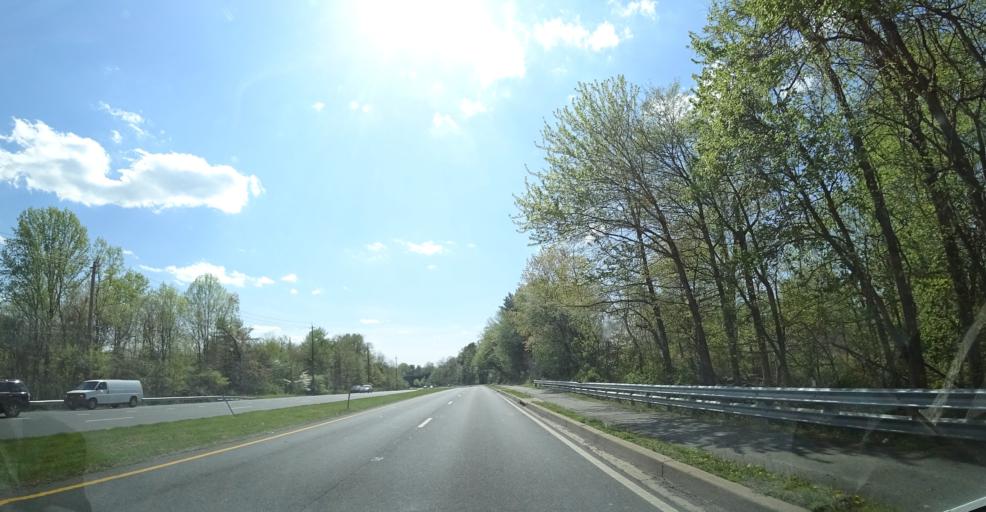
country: US
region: Maryland
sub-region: Montgomery County
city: Rockville
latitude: 39.0892
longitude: -77.1313
